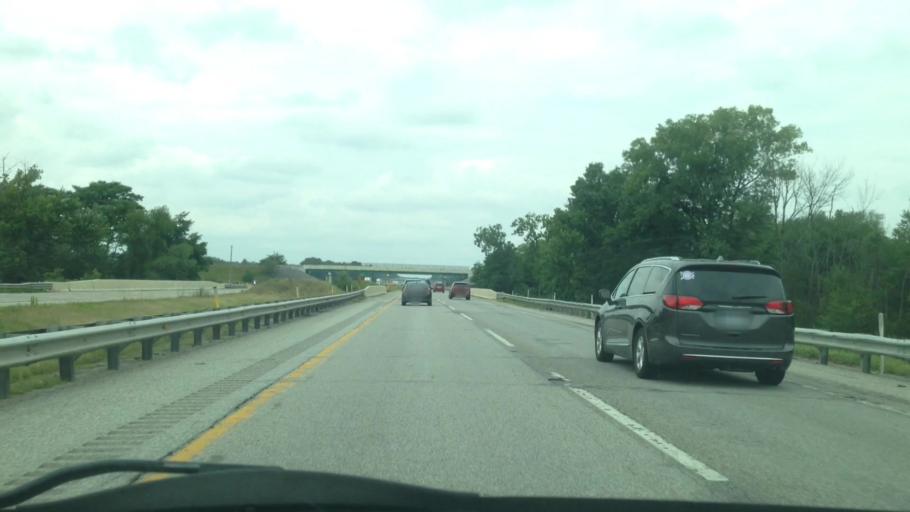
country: US
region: Michigan
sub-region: Saint Joseph County
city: White Pigeon
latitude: 41.7538
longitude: -85.5789
